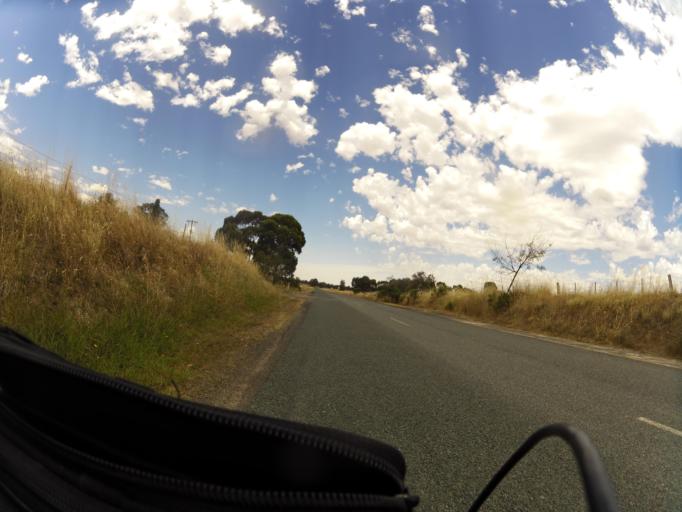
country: AU
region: Victoria
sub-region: Greater Shepparton
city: Shepparton
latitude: -36.6318
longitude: 145.2107
